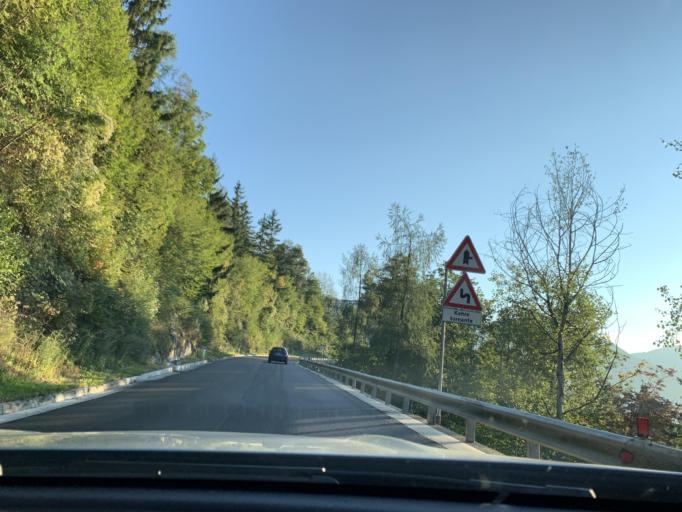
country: IT
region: Trentino-Alto Adige
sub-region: Bolzano
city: Fie Allo Sciliar
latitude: 46.5014
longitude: 11.4699
